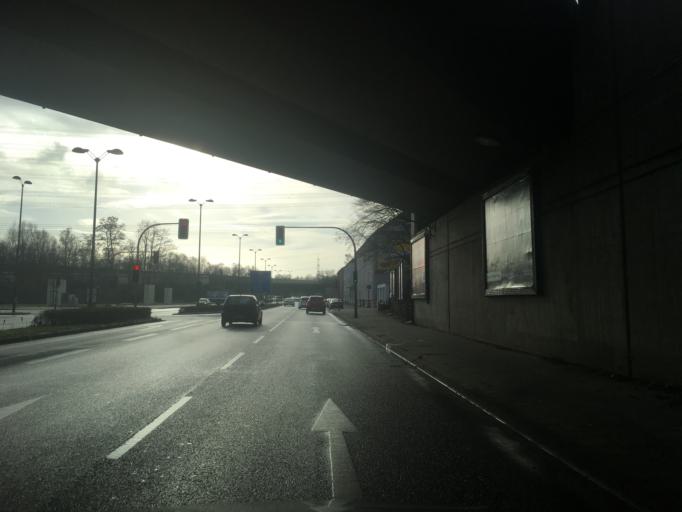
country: DE
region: North Rhine-Westphalia
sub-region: Regierungsbezirk Munster
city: Bottrop
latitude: 51.5080
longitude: 6.9350
